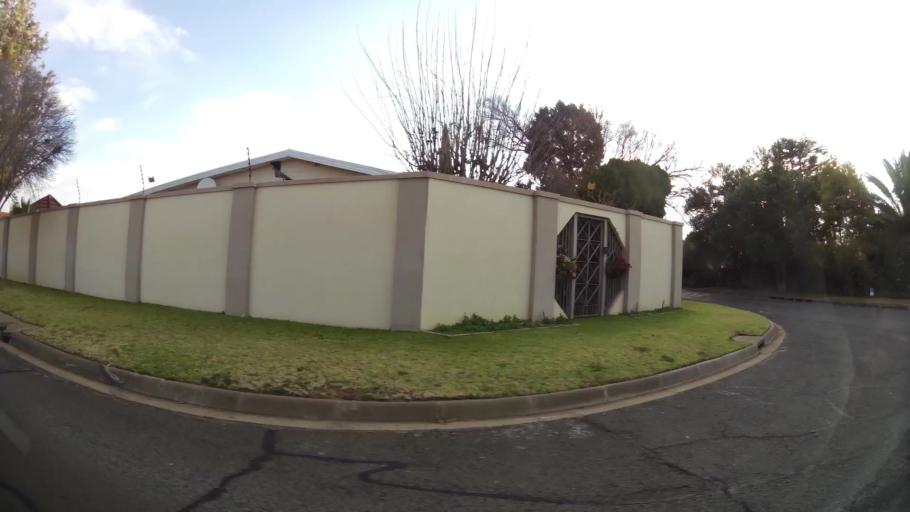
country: ZA
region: Orange Free State
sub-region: Mangaung Metropolitan Municipality
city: Bloemfontein
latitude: -29.1401
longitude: 26.1869
